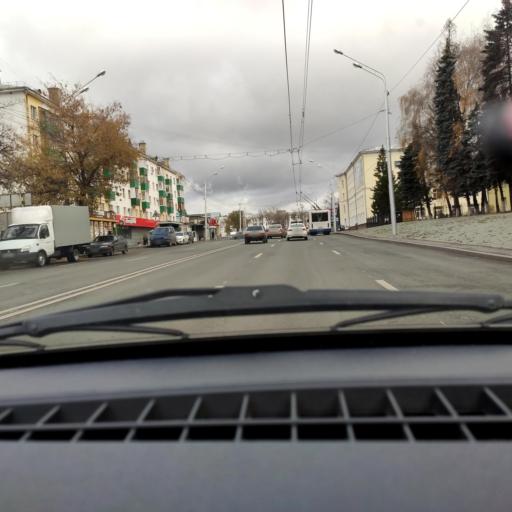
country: RU
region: Bashkortostan
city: Ufa
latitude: 54.7367
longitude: 55.9812
